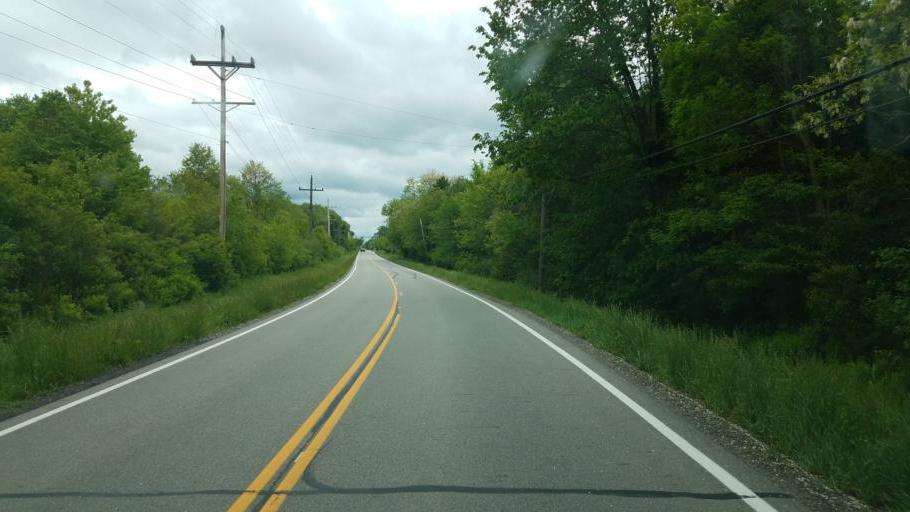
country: US
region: Ohio
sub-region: Geauga County
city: Burton
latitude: 41.4112
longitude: -81.1716
